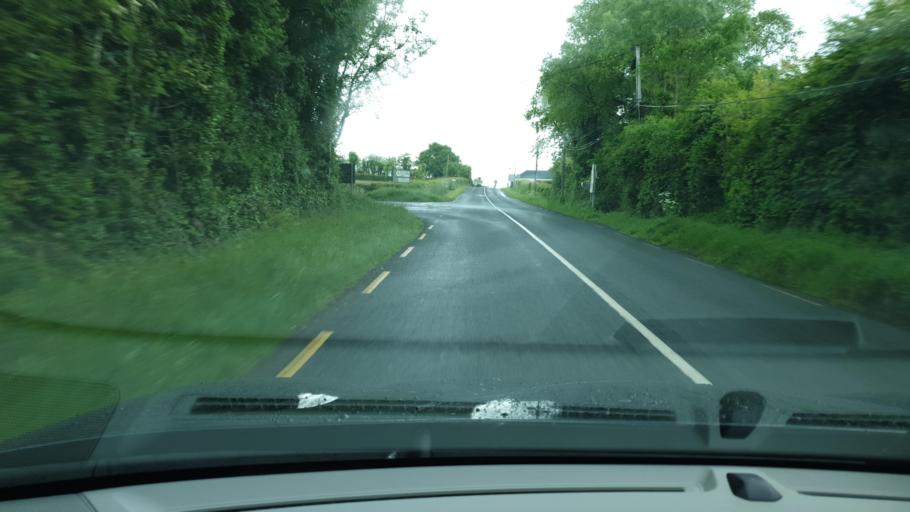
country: IE
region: Leinster
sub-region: Laois
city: Mountrath
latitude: 53.0657
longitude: -7.4076
